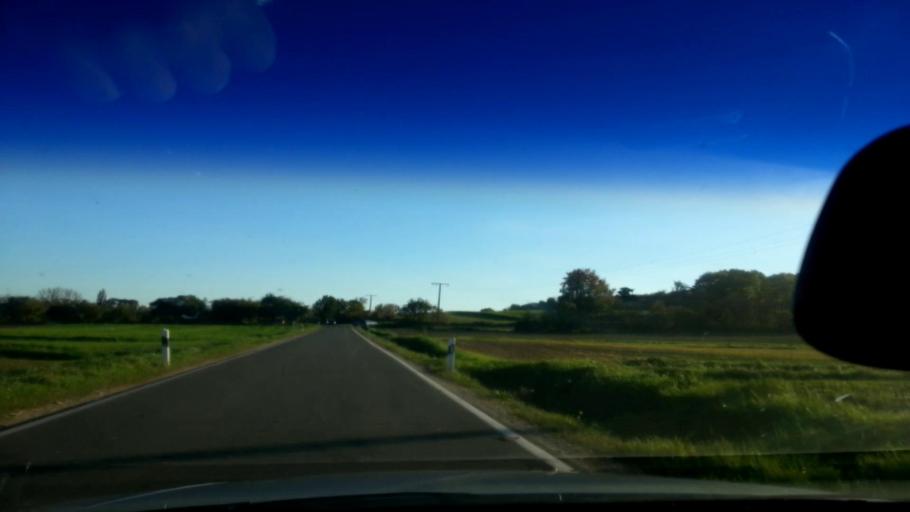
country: DE
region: Bavaria
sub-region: Upper Franconia
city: Rattelsdorf
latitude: 50.0136
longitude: 10.8724
